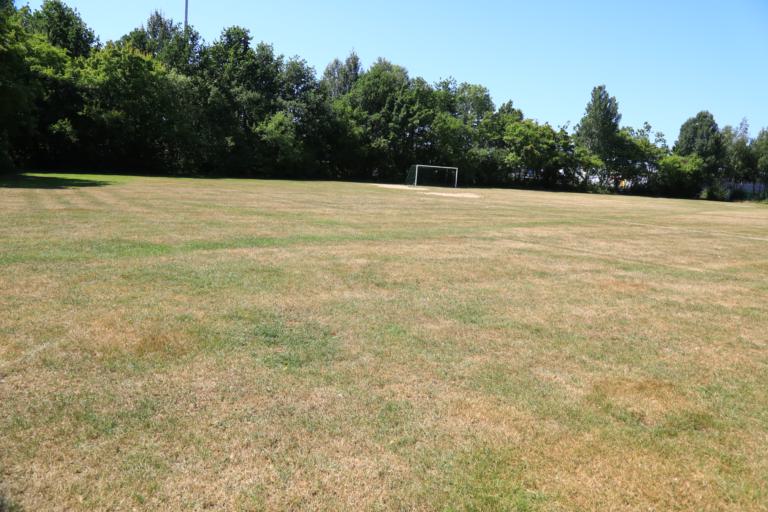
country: SE
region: Halland
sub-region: Halmstads Kommun
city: Fyllinge
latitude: 56.6661
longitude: 12.9091
